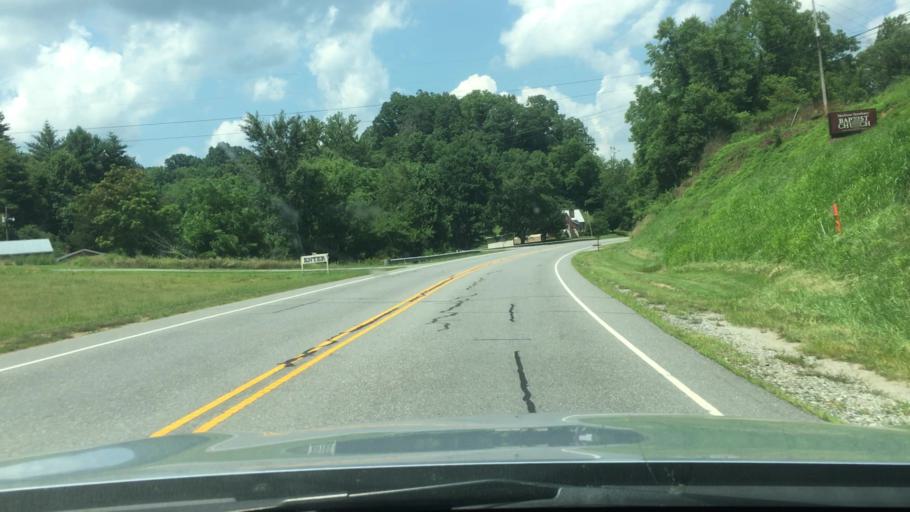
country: US
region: North Carolina
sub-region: Madison County
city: Marshall
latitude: 35.8091
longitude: -82.6575
